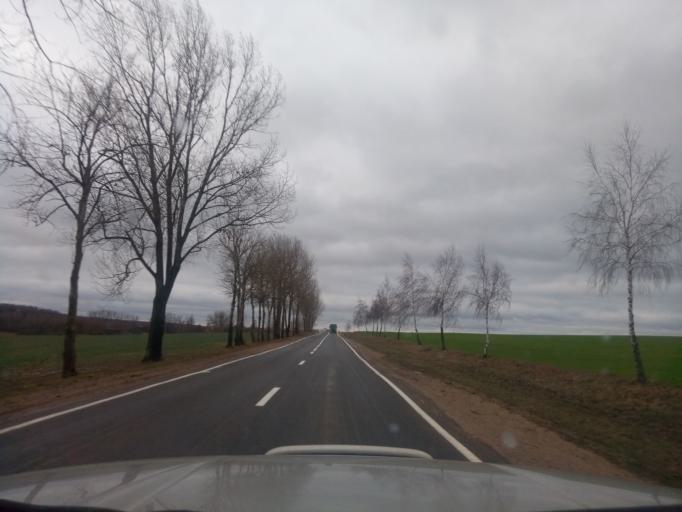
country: BY
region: Minsk
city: Kapyl'
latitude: 53.1815
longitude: 27.1737
